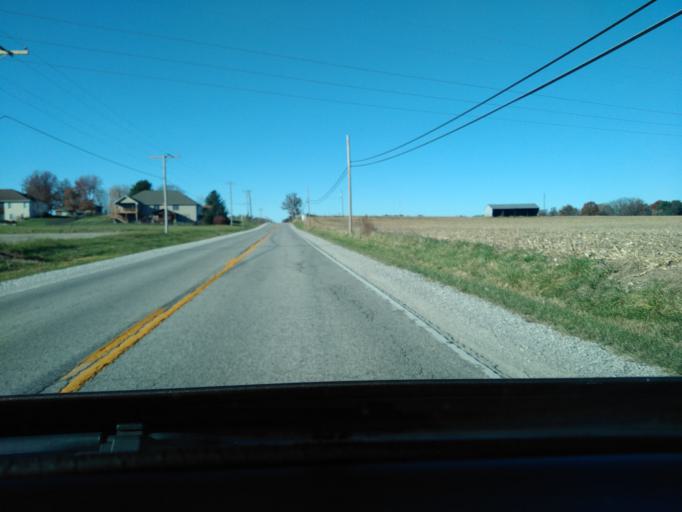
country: US
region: Illinois
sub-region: Bond County
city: Greenville
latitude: 38.9020
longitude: -89.3842
